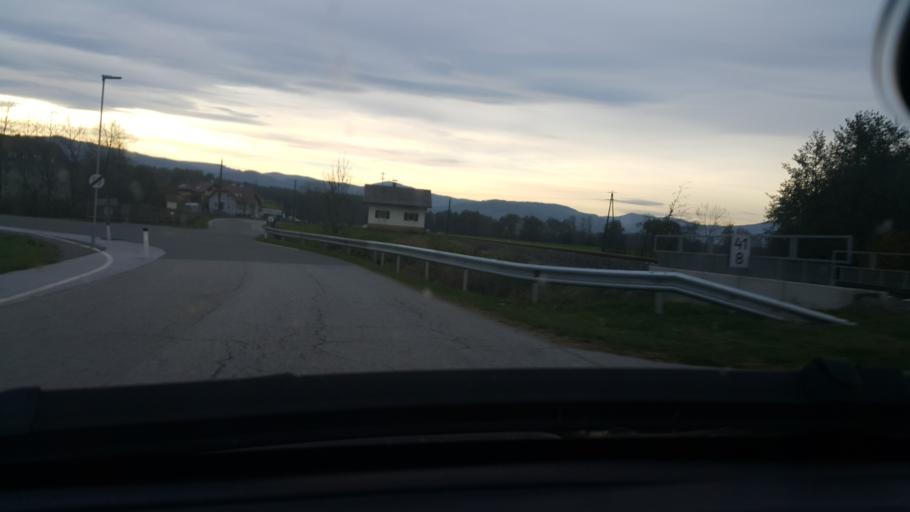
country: AT
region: Styria
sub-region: Politischer Bezirk Deutschlandsberg
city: Sankt Martin im Sulmtal
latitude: 46.7500
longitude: 15.2795
